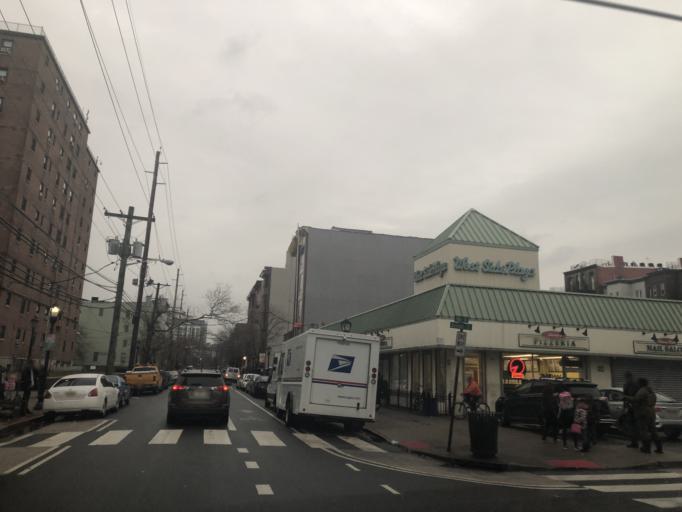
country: US
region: New Jersey
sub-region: Hudson County
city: Hoboken
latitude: 40.7417
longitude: -74.0403
